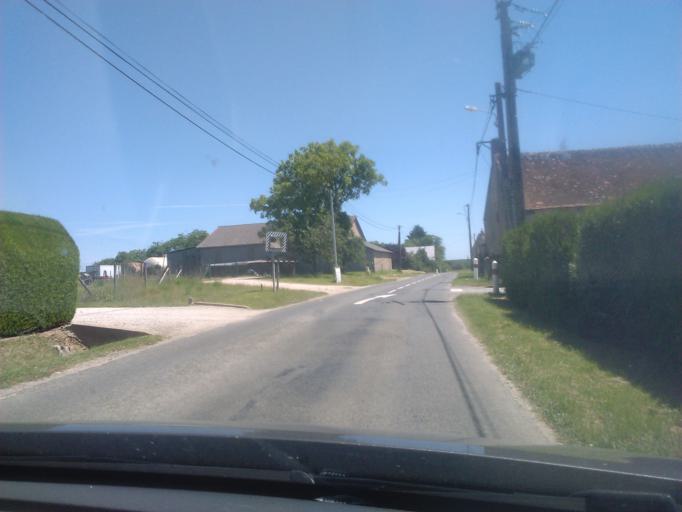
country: FR
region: Centre
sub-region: Departement du Loir-et-Cher
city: Saint-Sulpice-de-Pommeray
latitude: 47.6195
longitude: 1.2157
